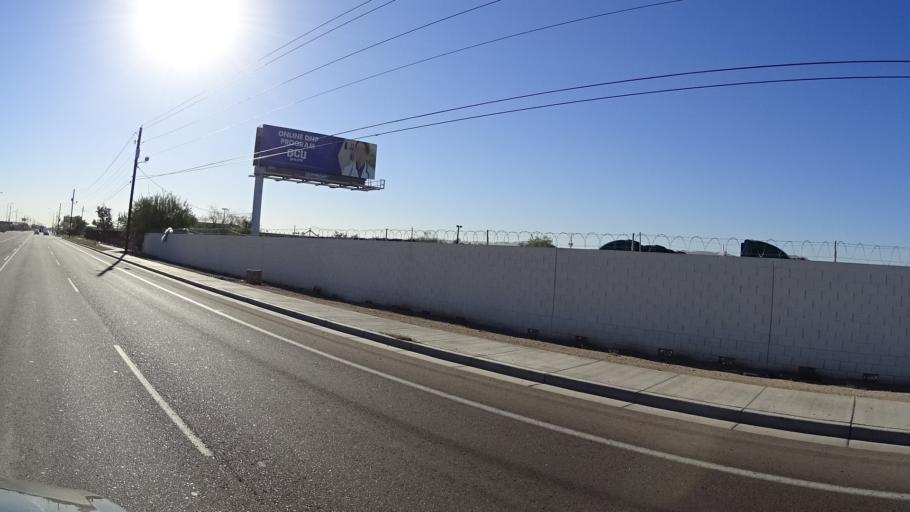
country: US
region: Arizona
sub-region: Maricopa County
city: Laveen
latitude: 33.4225
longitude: -112.1459
